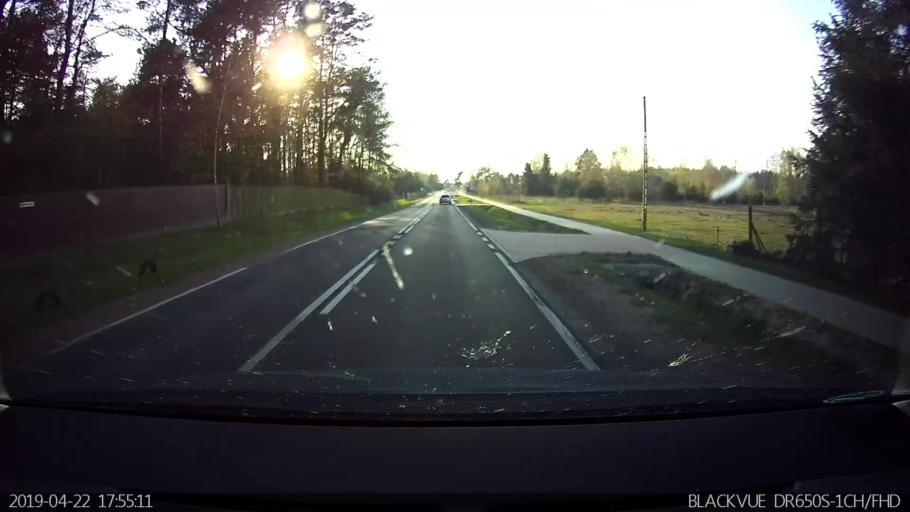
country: PL
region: Masovian Voivodeship
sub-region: Powiat wegrowski
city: Stoczek
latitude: 52.4609
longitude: 21.9221
